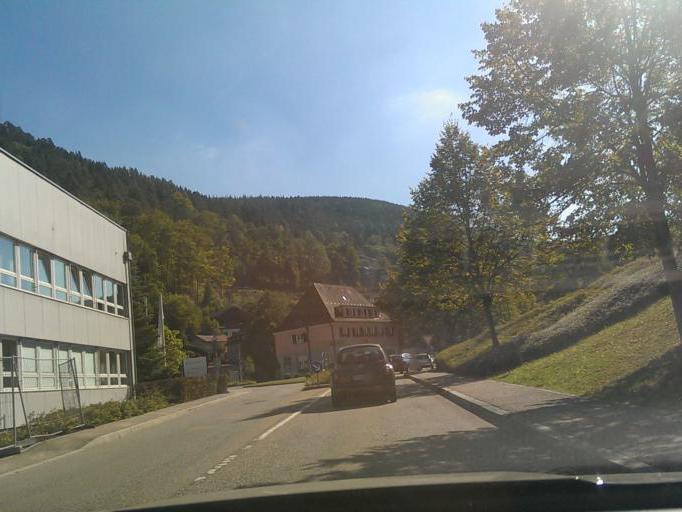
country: DE
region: Baden-Wuerttemberg
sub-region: Karlsruhe Region
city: Bad Wildbad
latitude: 48.7568
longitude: 8.5522
